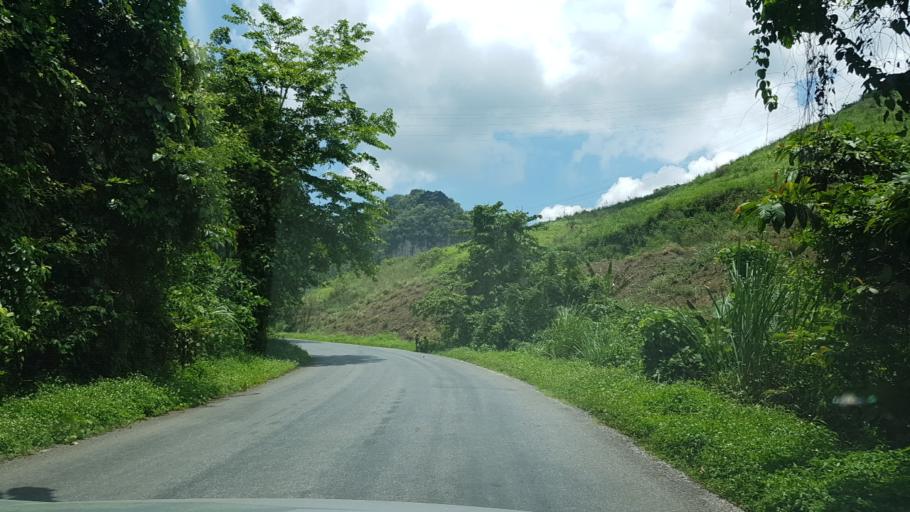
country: LA
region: Vientiane
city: Muang Kasi
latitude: 19.1393
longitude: 102.2911
